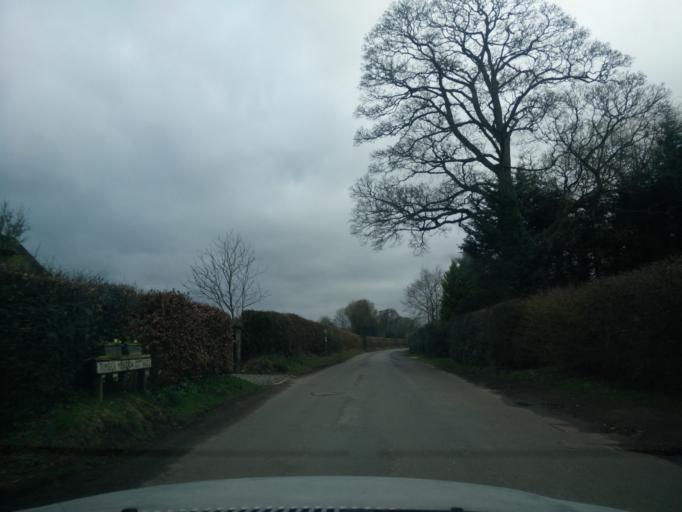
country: GB
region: England
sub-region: Buckinghamshire
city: Amersham
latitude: 51.6807
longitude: -0.6623
